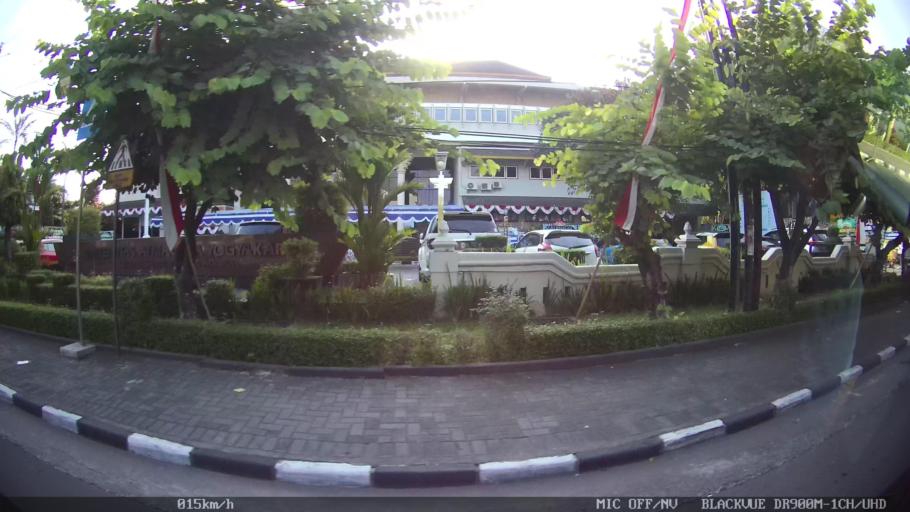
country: ID
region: Daerah Istimewa Yogyakarta
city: Depok
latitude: -7.7806
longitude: 110.4145
